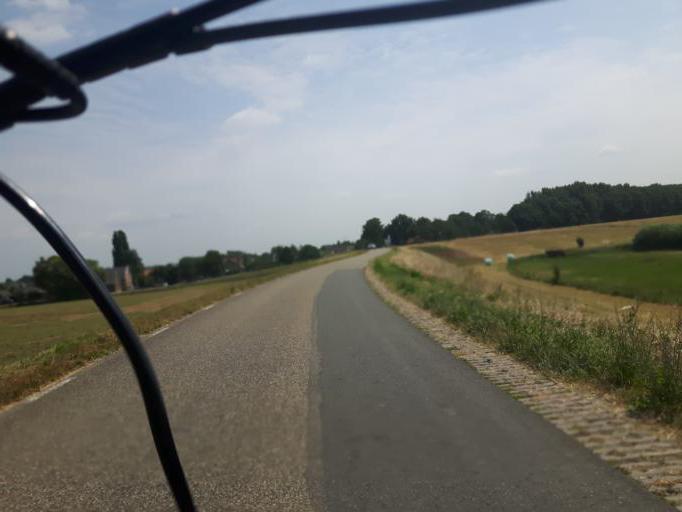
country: NL
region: South Holland
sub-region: Gemeente Leerdam
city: Leerdam
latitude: 51.8275
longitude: 5.1156
